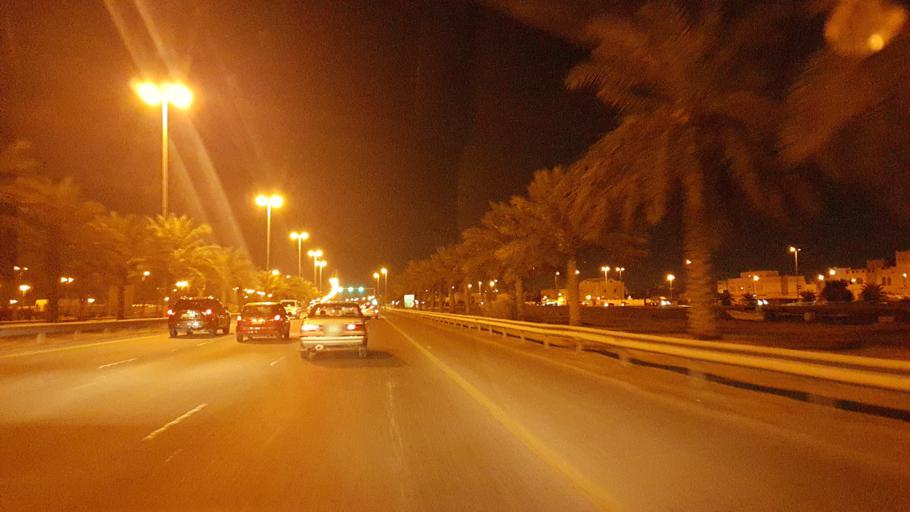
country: BH
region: Muharraq
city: Al Hadd
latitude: 26.2475
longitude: 50.6587
